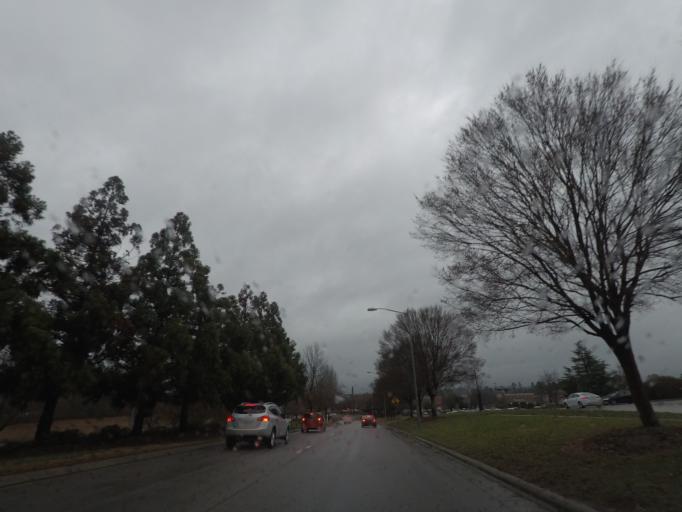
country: US
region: North Carolina
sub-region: Durham County
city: Durham
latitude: 35.9020
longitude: -78.9437
